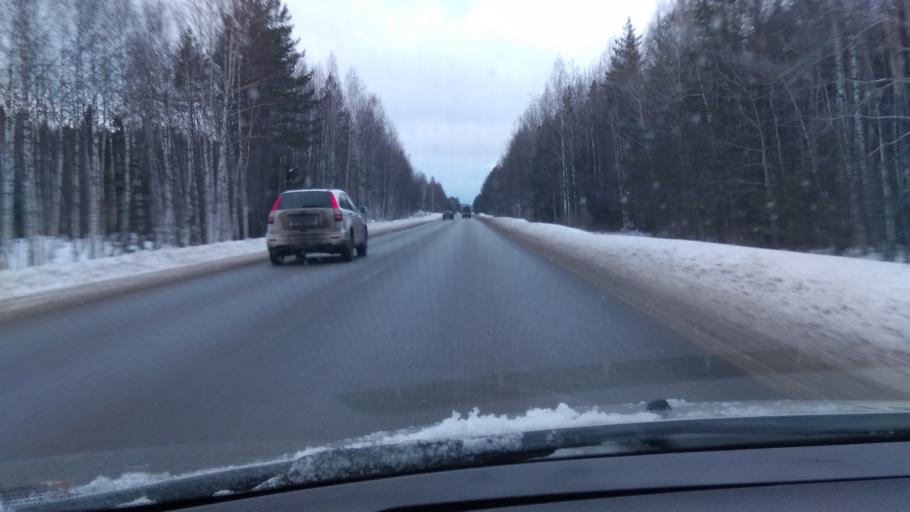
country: RU
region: Sverdlovsk
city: Iset'
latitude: 57.1119
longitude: 60.3379
